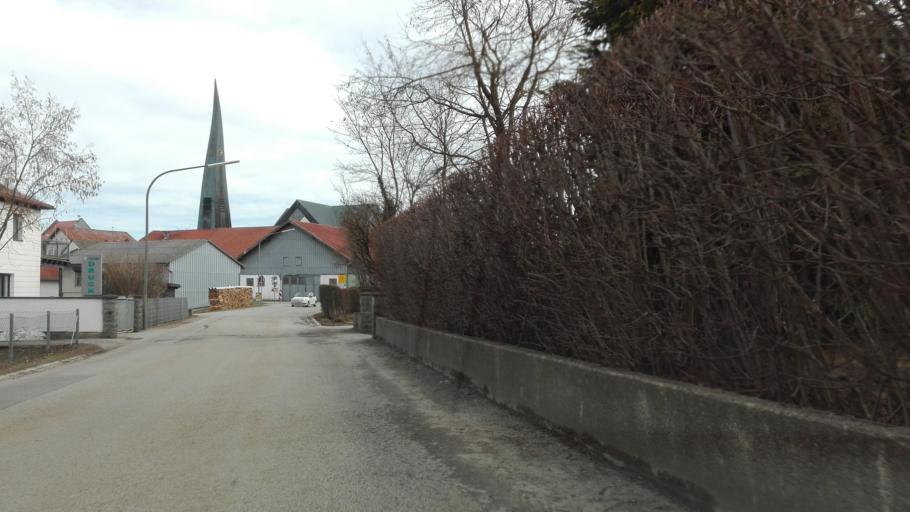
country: DE
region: Bavaria
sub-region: Lower Bavaria
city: Wegscheid
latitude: 48.6026
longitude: 13.7844
